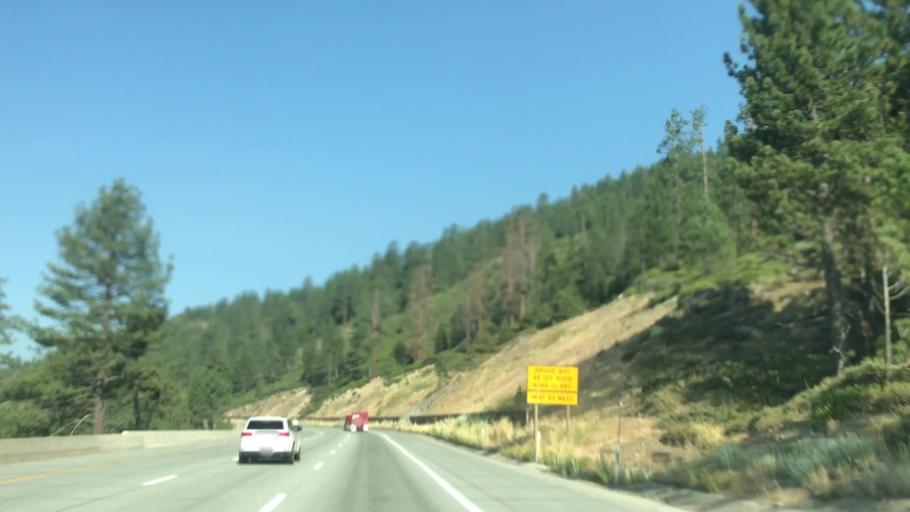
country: US
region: California
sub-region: Nevada County
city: Truckee
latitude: 39.3320
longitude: -120.2555
